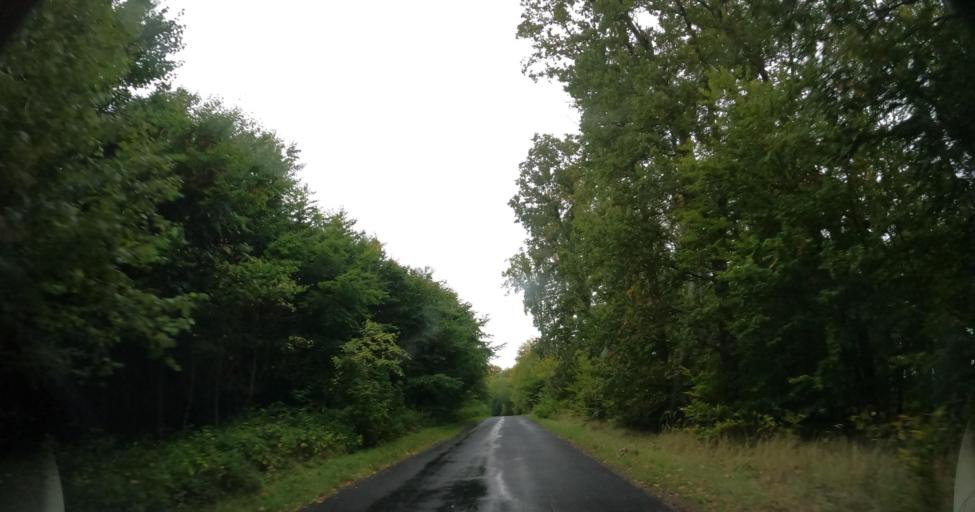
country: PL
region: West Pomeranian Voivodeship
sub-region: Powiat gryfinski
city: Banie
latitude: 53.0530
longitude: 14.7427
